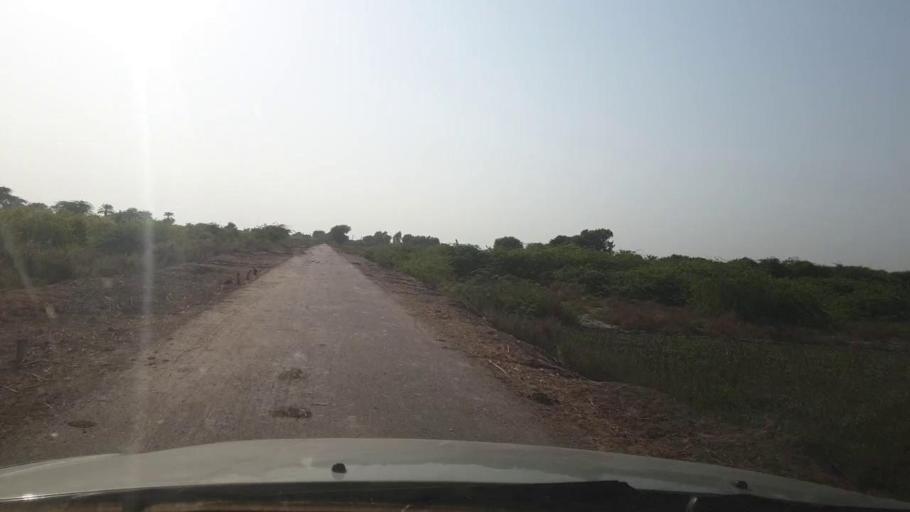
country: PK
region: Sindh
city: Tando Ghulam Ali
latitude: 25.1892
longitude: 68.9463
